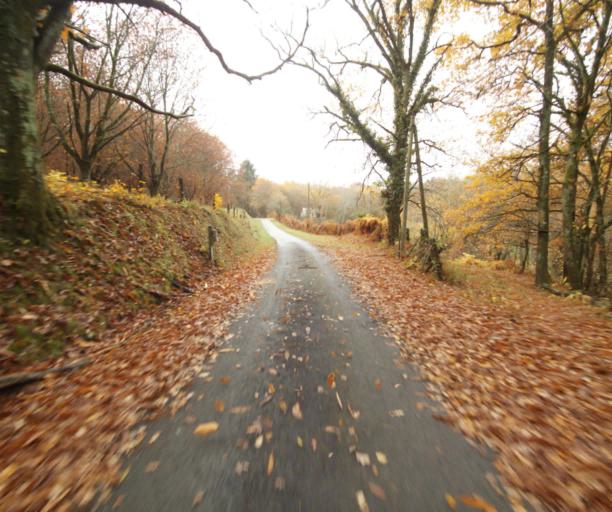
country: FR
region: Limousin
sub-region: Departement de la Correze
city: Cornil
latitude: 45.1905
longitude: 1.6370
